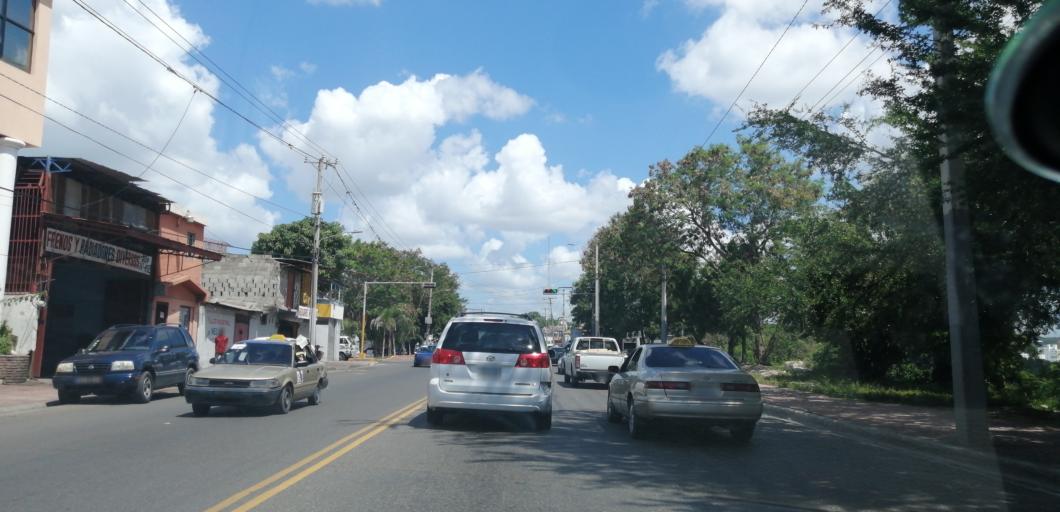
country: DO
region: Santiago
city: Santiago de los Caballeros
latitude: 19.4355
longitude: -70.6972
